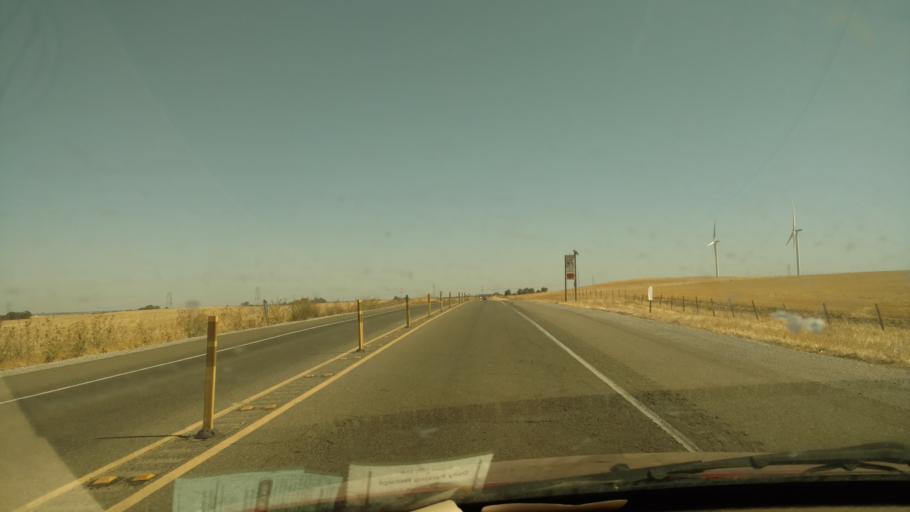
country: US
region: California
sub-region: Solano County
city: Rio Vista
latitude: 38.1835
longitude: -121.7659
